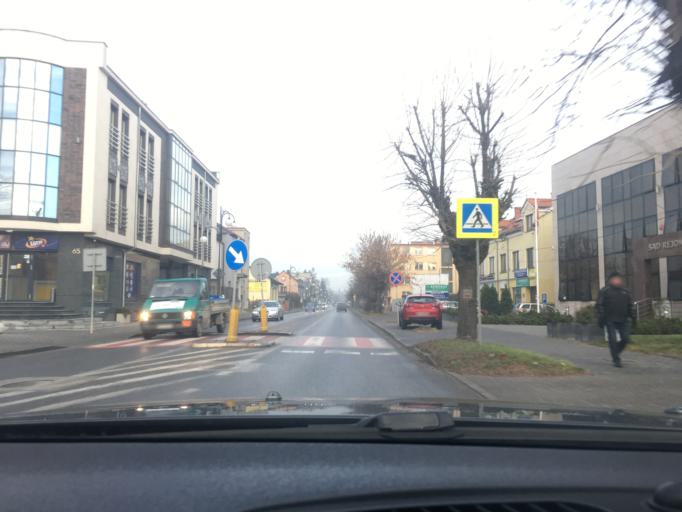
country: PL
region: Swietokrzyskie
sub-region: Powiat jedrzejowski
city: Jedrzejow
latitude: 50.6437
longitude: 20.2967
